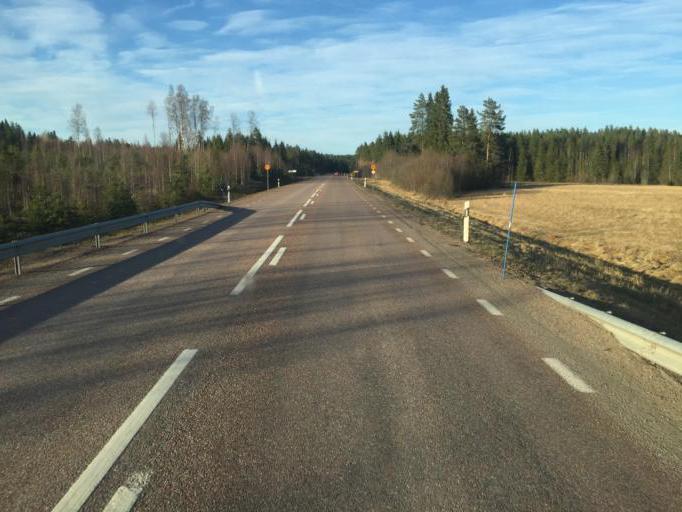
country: SE
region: Dalarna
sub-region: Gagnefs Kommun
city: Mockfjard
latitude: 60.5141
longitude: 14.9729
